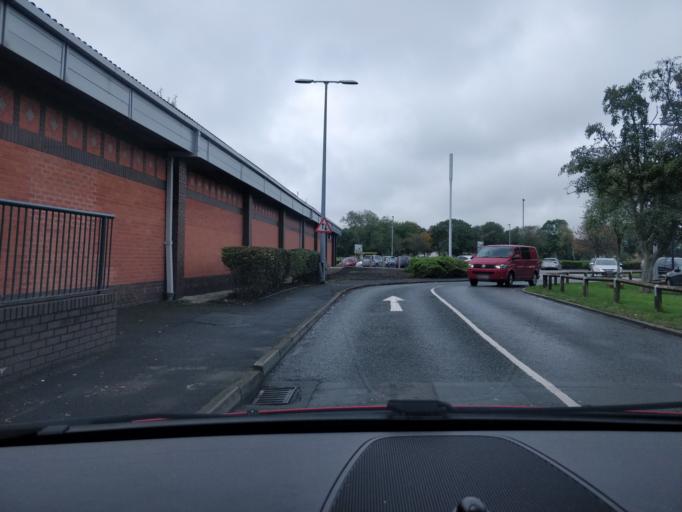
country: GB
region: England
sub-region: Sefton
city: Southport
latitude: 53.6346
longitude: -2.9689
